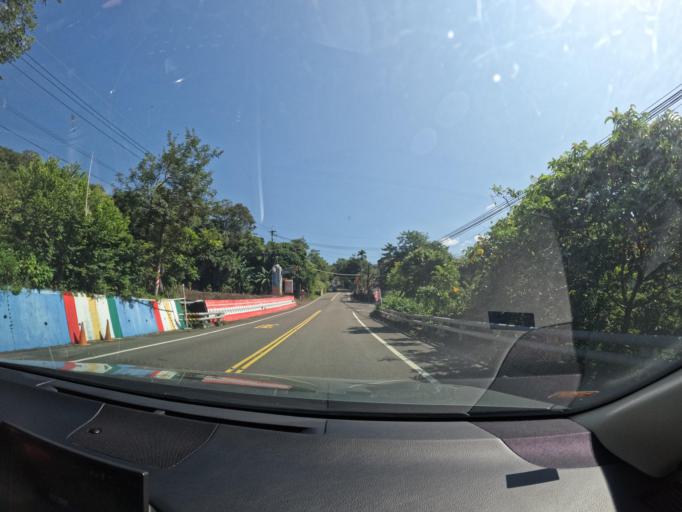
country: TW
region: Taiwan
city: Yujing
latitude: 23.1325
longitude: 120.7209
